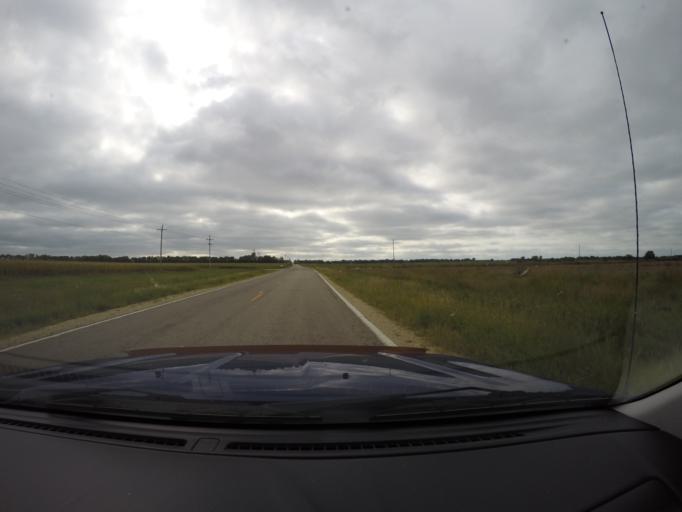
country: US
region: Kansas
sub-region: Dickinson County
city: Herington
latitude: 38.7977
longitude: -96.9443
